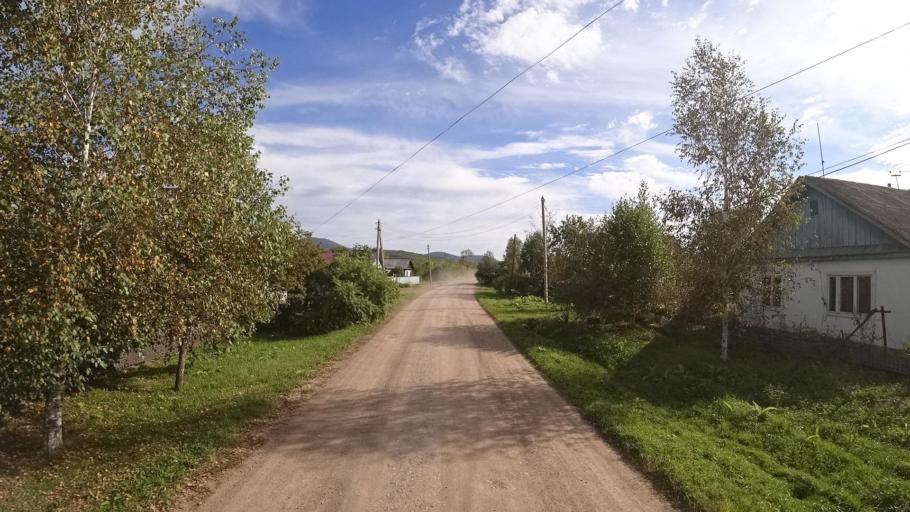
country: RU
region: Primorskiy
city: Dostoyevka
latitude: 44.2995
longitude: 133.4599
